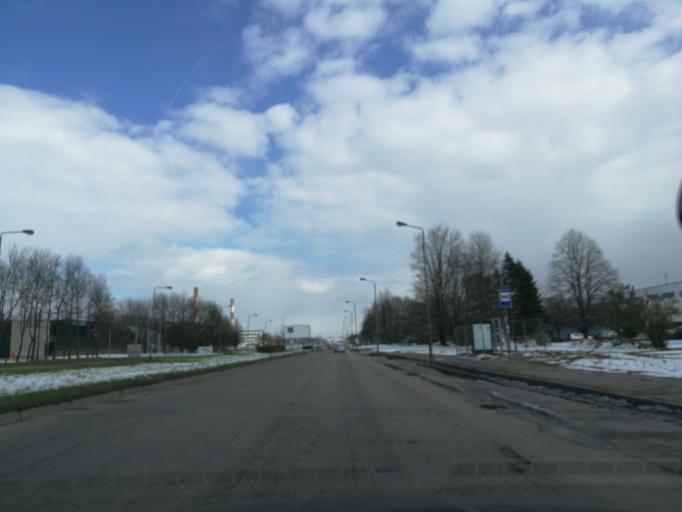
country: LT
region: Kauno apskritis
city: Dainava (Kaunas)
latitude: 54.9187
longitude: 23.9928
